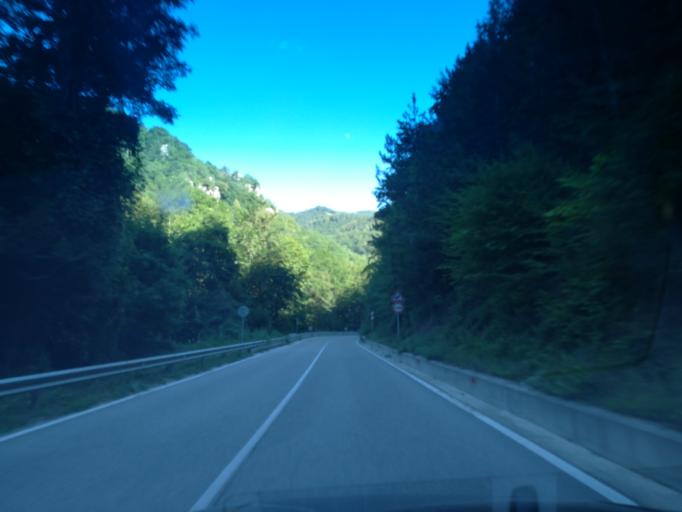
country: BG
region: Smolyan
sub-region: Obshtina Chepelare
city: Chepelare
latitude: 41.8077
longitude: 24.7079
